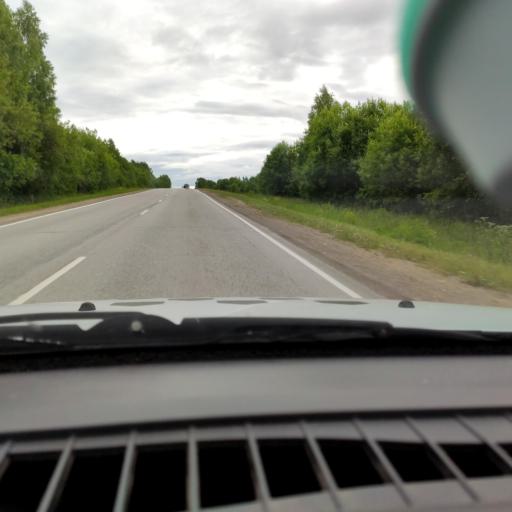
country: RU
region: Perm
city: Lys'va
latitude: 58.1380
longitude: 57.7402
